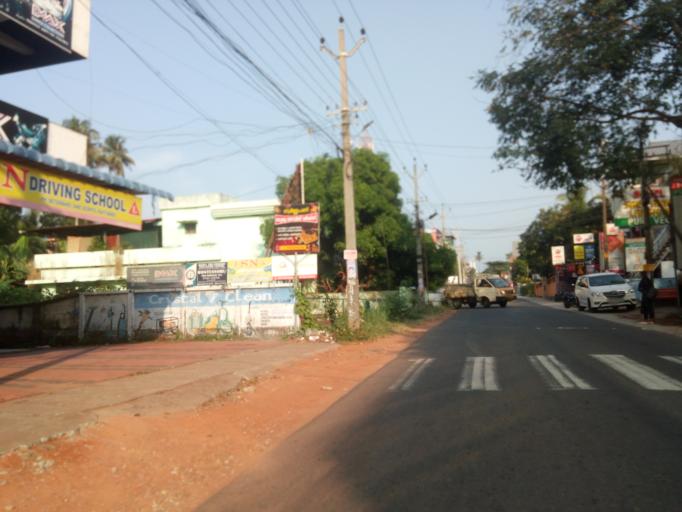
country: IN
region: Kerala
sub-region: Thrissur District
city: Irinjalakuda
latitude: 10.3431
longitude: 76.2150
